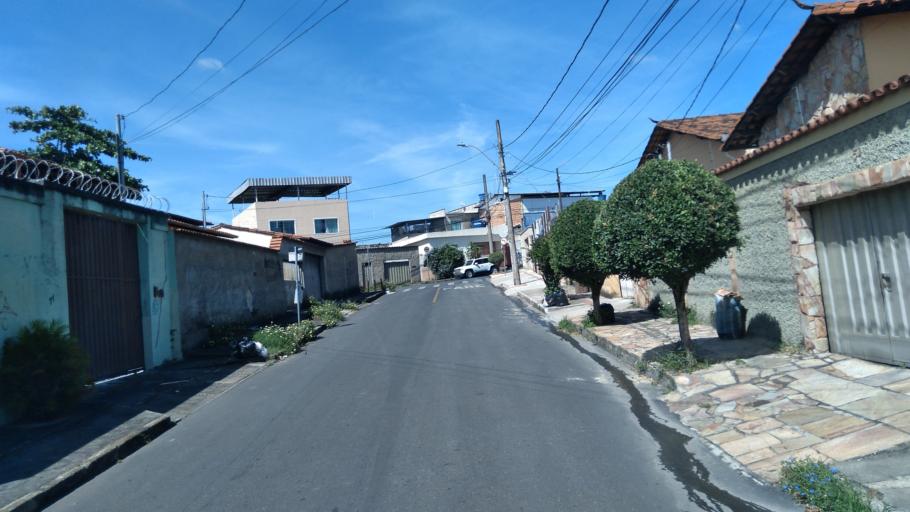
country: BR
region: Minas Gerais
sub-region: Contagem
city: Contagem
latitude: -19.8908
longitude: -44.0130
